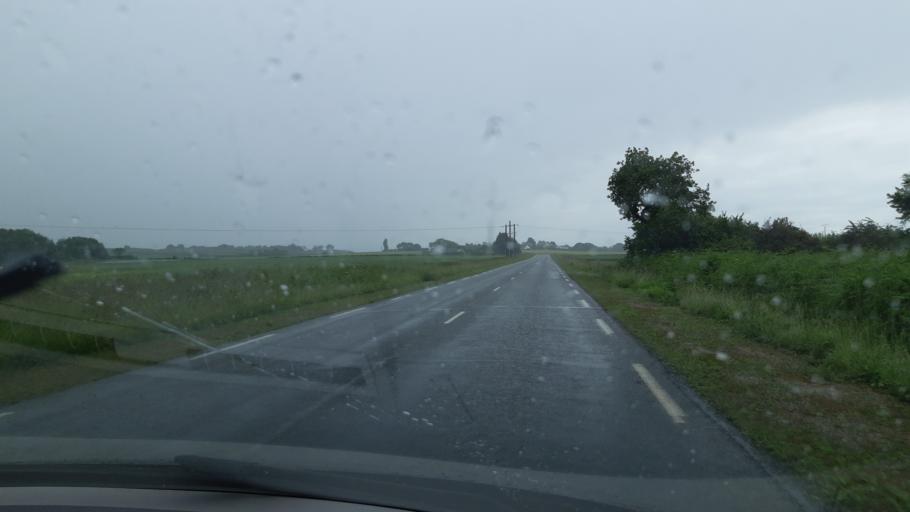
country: FR
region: Brittany
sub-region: Departement du Finistere
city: Plougoulm
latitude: 48.6295
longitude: -4.0550
